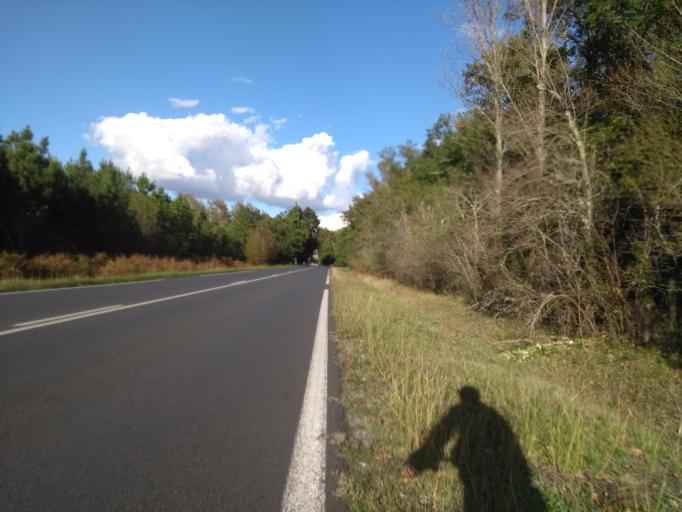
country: FR
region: Aquitaine
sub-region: Departement de la Gironde
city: Cestas
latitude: 44.7211
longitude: -0.6864
